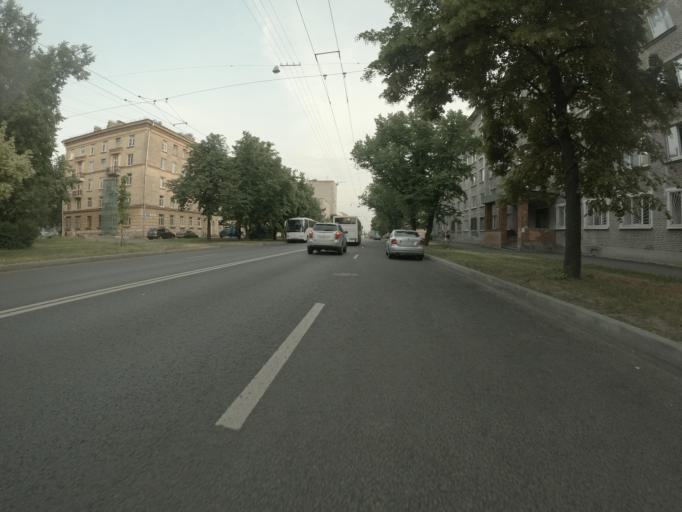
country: RU
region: Leningrad
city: Kalininskiy
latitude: 59.9757
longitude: 30.3911
